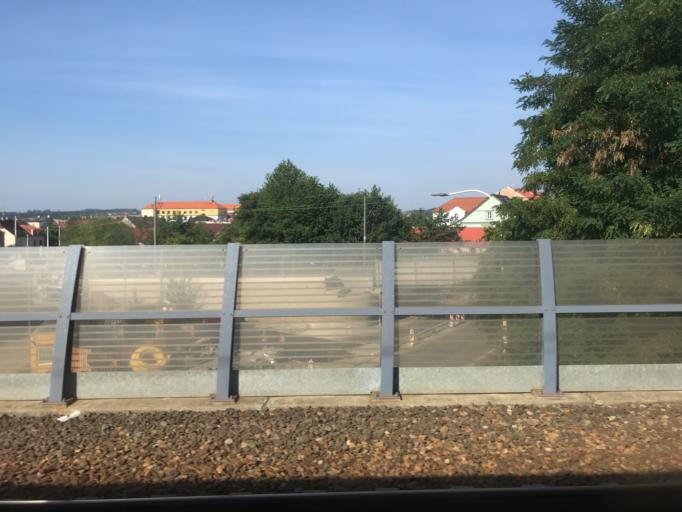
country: CZ
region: Jihocesky
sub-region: Okres Tabor
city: Tabor
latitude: 49.4107
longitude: 14.6811
